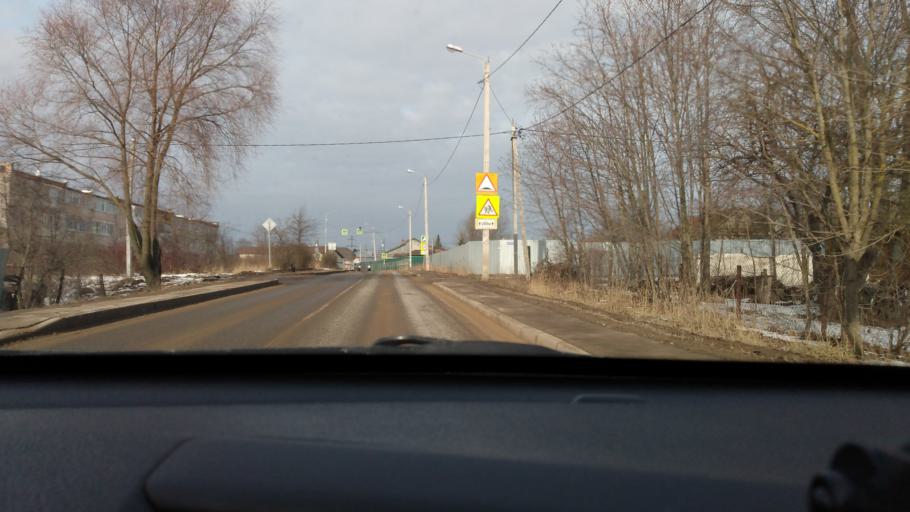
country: RU
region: Moskovskaya
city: Nakhabino
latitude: 55.8913
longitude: 37.1826
